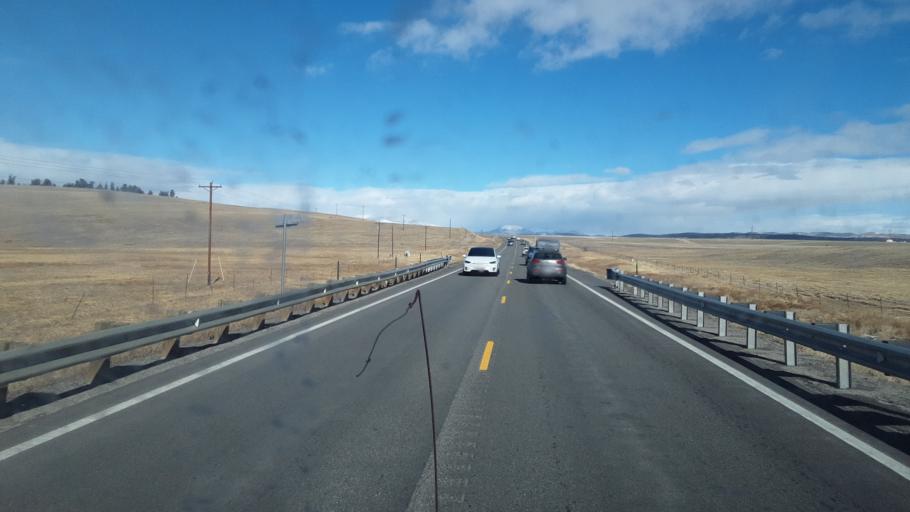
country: US
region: Colorado
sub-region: Park County
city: Fairplay
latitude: 39.0723
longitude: -105.9741
